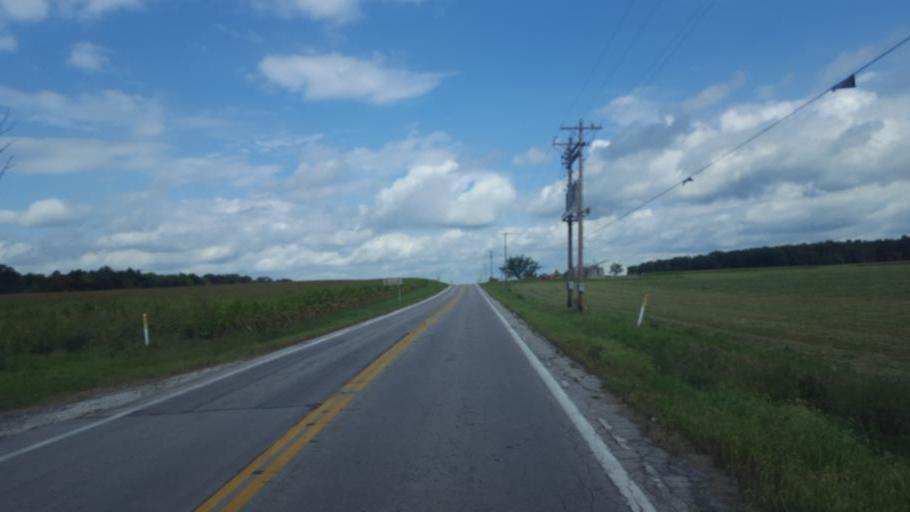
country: US
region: Ohio
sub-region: Seneca County
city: Tiffin
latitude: 41.0816
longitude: -83.0152
